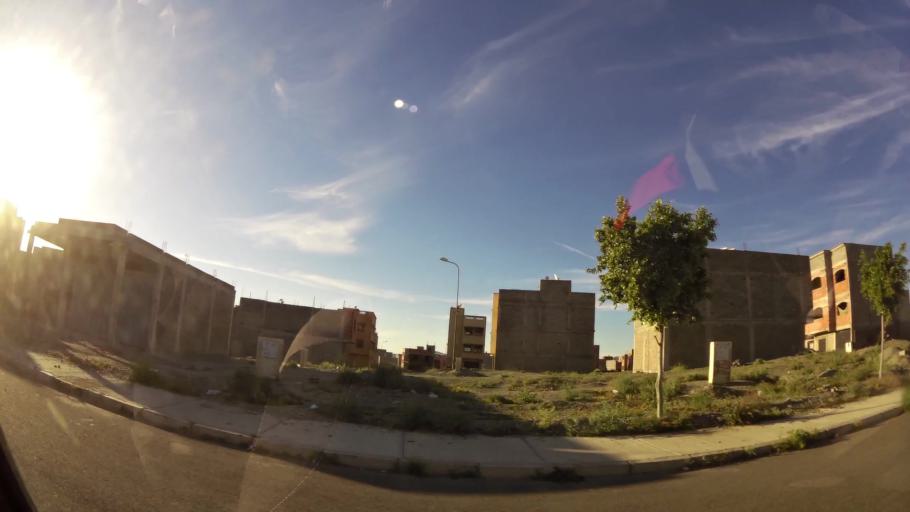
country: MA
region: Marrakech-Tensift-Al Haouz
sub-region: Marrakech
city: Marrakesh
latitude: 31.7672
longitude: -8.1064
